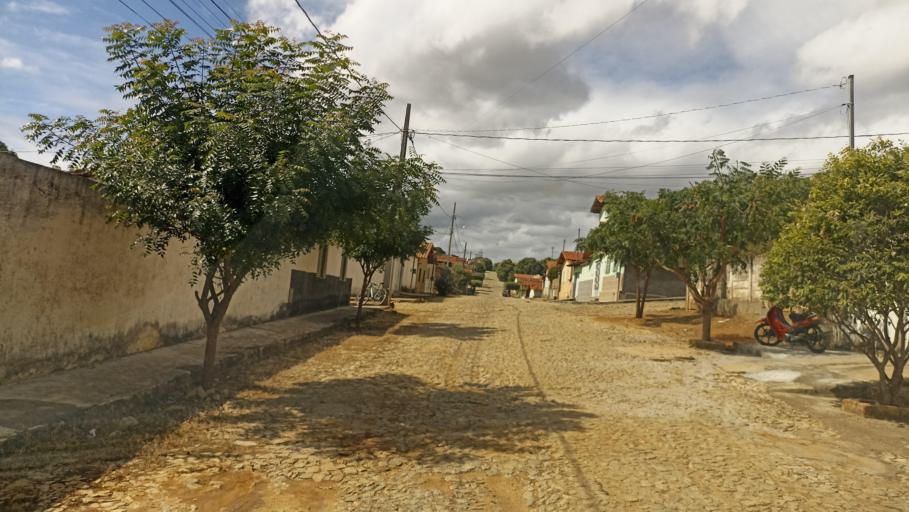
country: BR
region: Minas Gerais
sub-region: Jequitinhonha
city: Jequitinhonha
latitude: -16.4360
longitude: -41.0143
